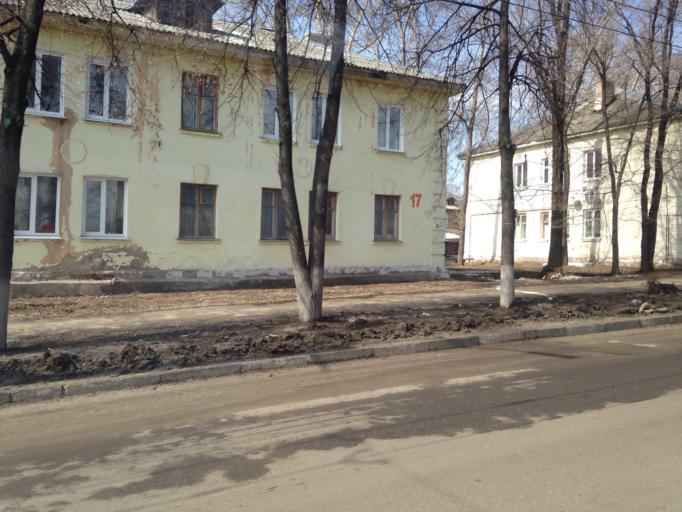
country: RU
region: Ulyanovsk
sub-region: Ulyanovskiy Rayon
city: Ulyanovsk
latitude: 54.3403
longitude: 48.5493
